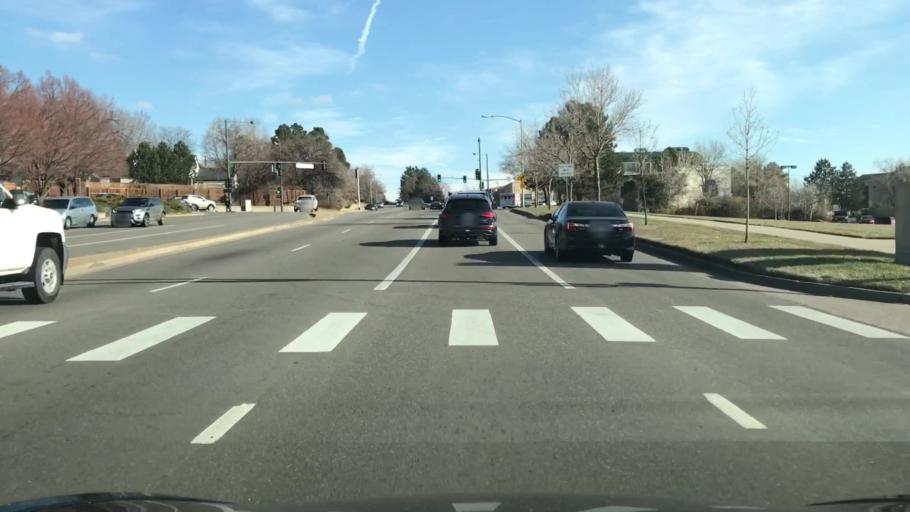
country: US
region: Colorado
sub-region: Arapahoe County
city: Glendale
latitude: 39.7113
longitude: -104.9381
